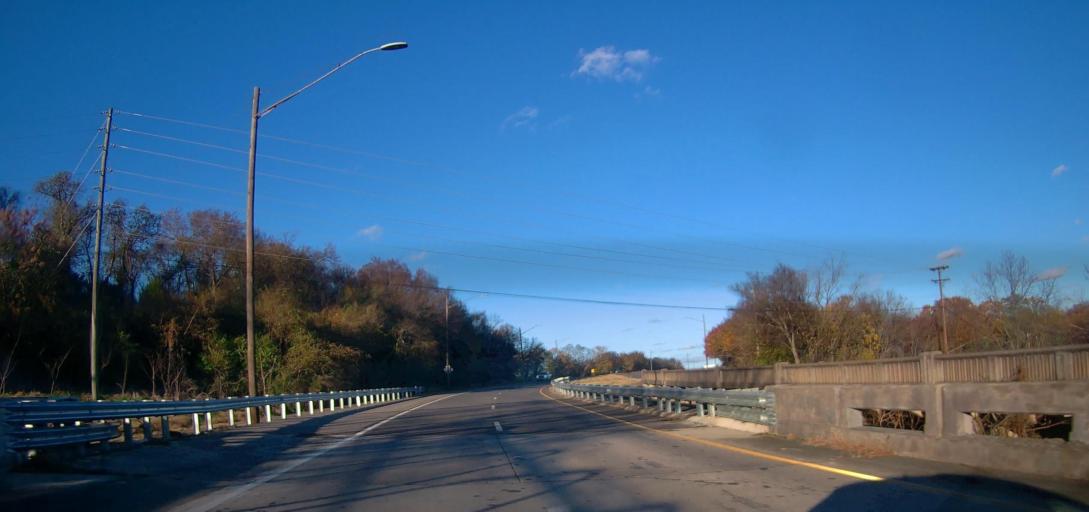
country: US
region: Alabama
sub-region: Jefferson County
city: Birmingham
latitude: 33.5629
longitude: -86.8193
